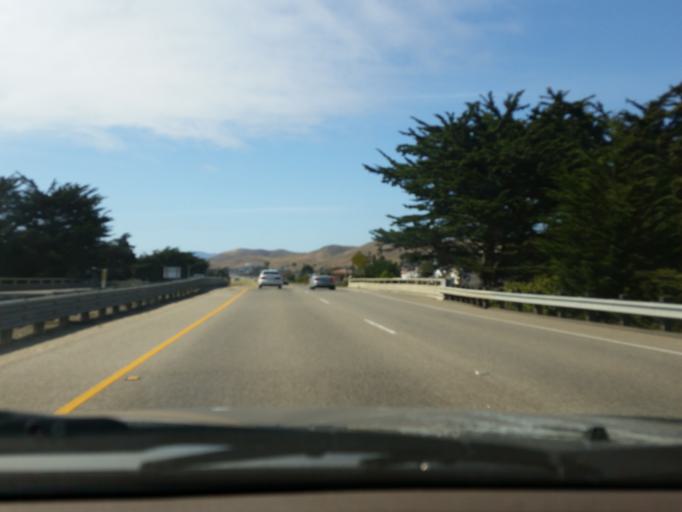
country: US
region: California
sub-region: San Luis Obispo County
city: Morro Bay
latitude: 35.3797
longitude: -120.8553
